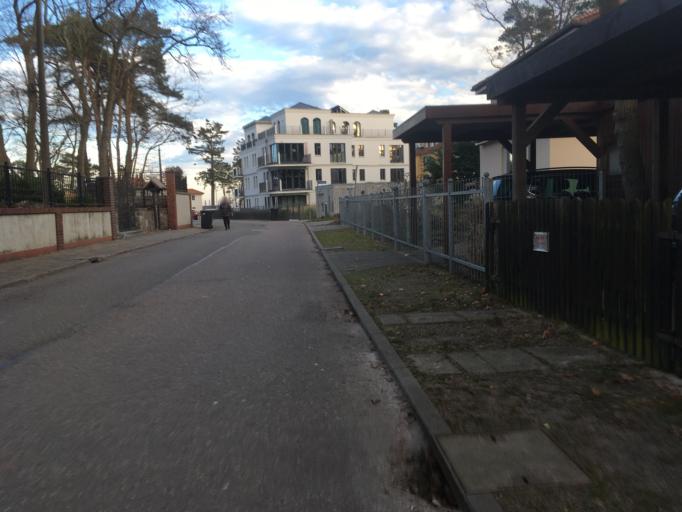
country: DE
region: Mecklenburg-Vorpommern
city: Ostseebad Sellin
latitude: 54.3629
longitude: 13.7111
